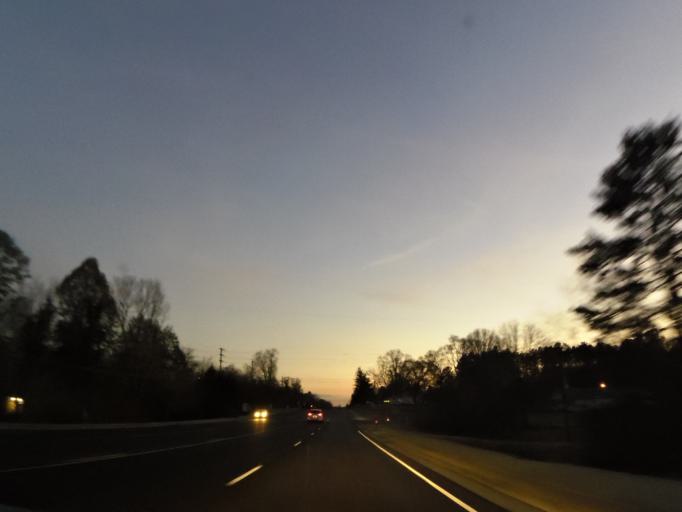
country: US
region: Georgia
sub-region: Whitfield County
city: Varnell
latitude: 34.8532
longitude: -84.9437
